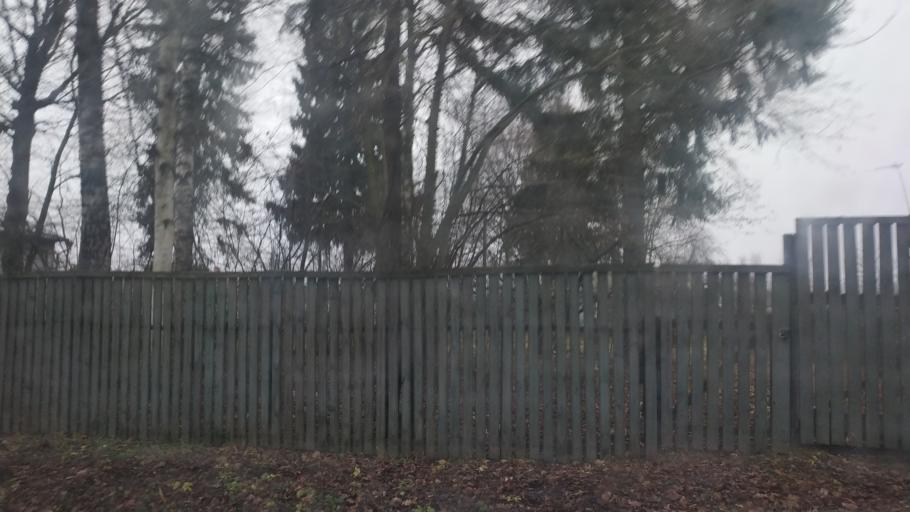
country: RU
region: Moskovskaya
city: Lugovaya
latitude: 56.0555
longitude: 37.4760
